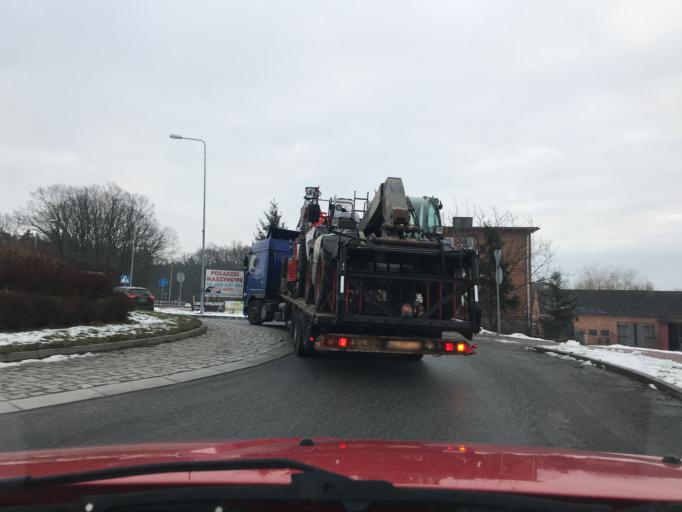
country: PL
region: Greater Poland Voivodeship
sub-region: Powiat pleszewski
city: Goluchow
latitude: 51.8481
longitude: 17.9373
